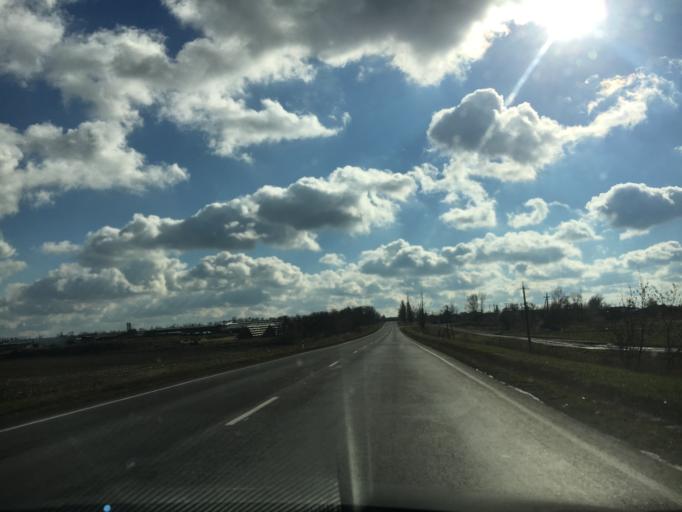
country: RU
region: Rostov
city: Matveyev Kurgan
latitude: 47.4989
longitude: 38.9113
